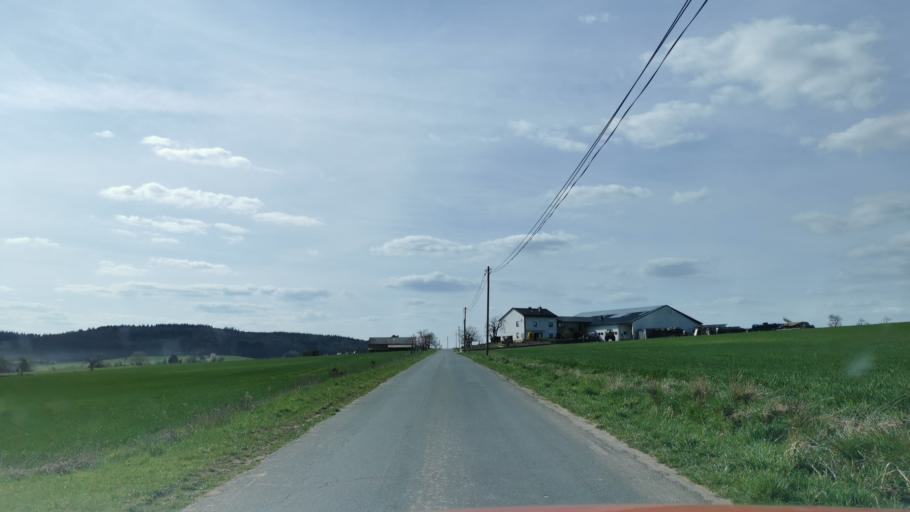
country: DE
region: Rheinland-Pfalz
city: Arenrath
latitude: 49.9618
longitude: 6.7473
